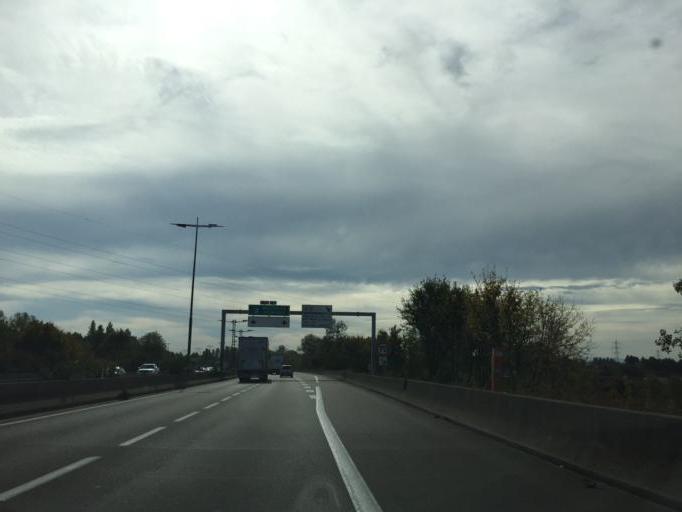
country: FR
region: Rhone-Alpes
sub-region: Departement du Rhone
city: Decines-Charpieu
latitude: 45.7876
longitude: 4.9560
